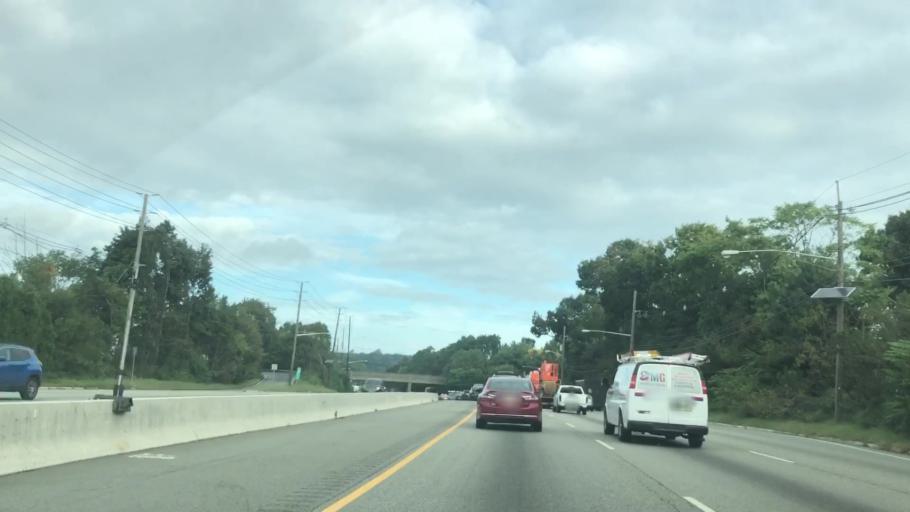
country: US
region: New Jersey
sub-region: Passaic County
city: Clifton
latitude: 40.8633
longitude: -74.1810
